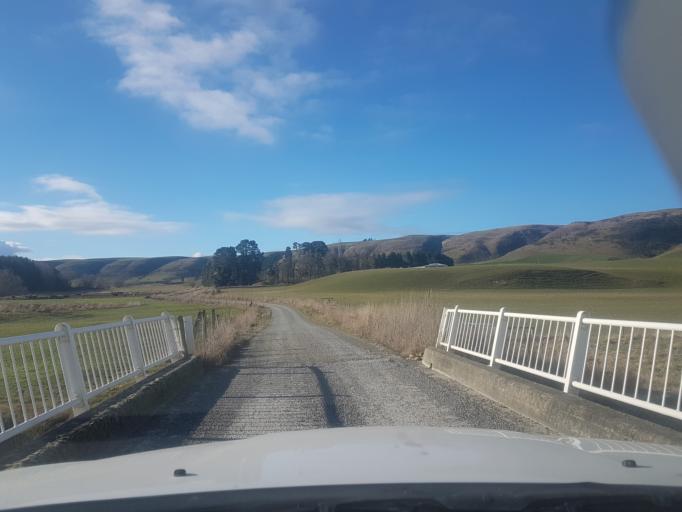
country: NZ
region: Canterbury
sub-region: Timaru District
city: Pleasant Point
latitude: -44.1768
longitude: 170.8604
